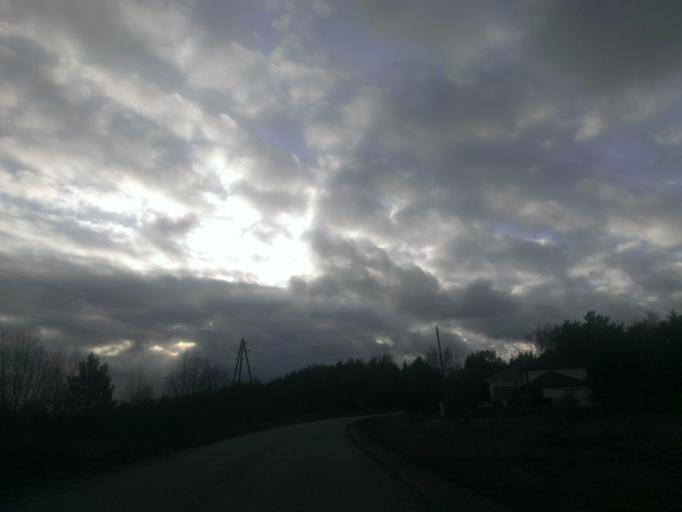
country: LV
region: Riga
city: Bolderaja
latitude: 57.0637
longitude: 24.0831
